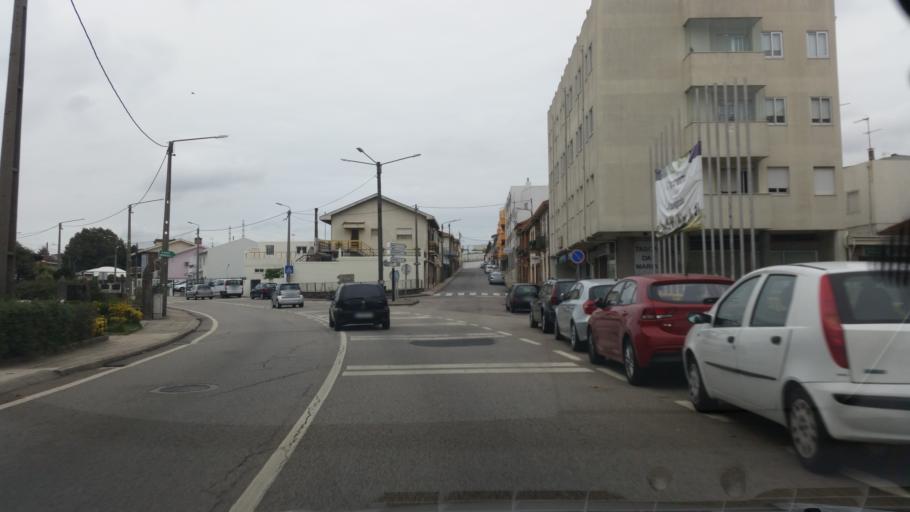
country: PT
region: Porto
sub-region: Valongo
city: Ermesinde
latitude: 41.2256
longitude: -8.5543
